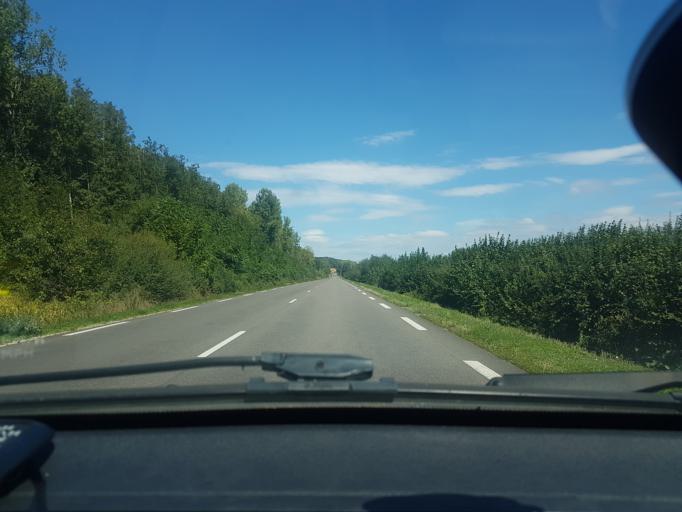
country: FR
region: Franche-Comte
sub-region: Departement de la Haute-Saone
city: Gray-la-Ville
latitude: 47.4360
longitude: 5.5421
